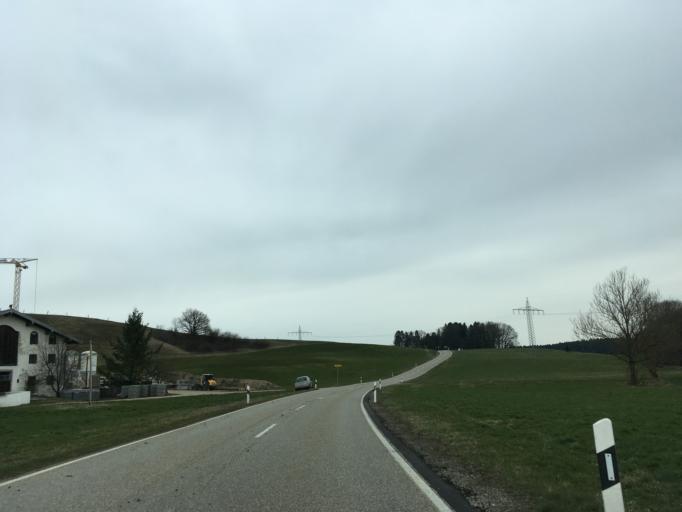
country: DE
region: Bavaria
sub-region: Upper Bavaria
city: Schnaitsee
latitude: 48.0650
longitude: 12.3810
